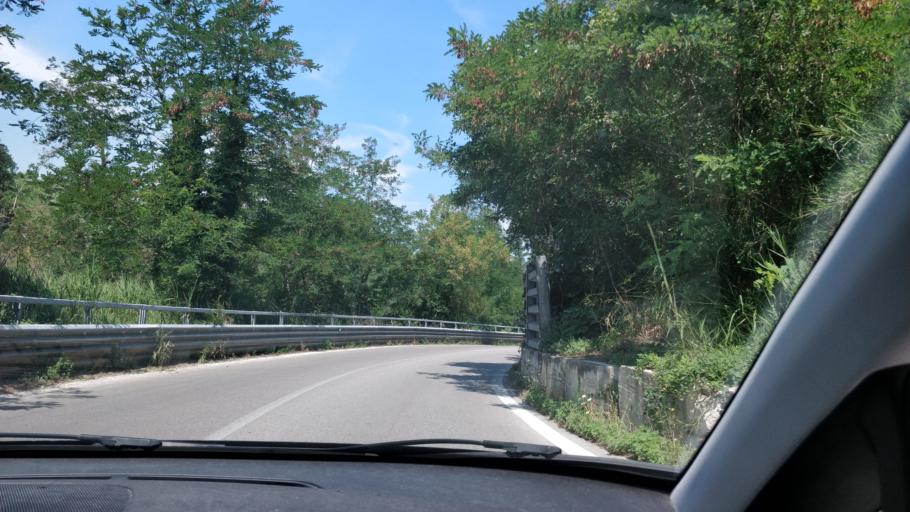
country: IT
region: Abruzzo
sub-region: Provincia di Chieti
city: Ortona
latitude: 42.3391
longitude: 14.4113
